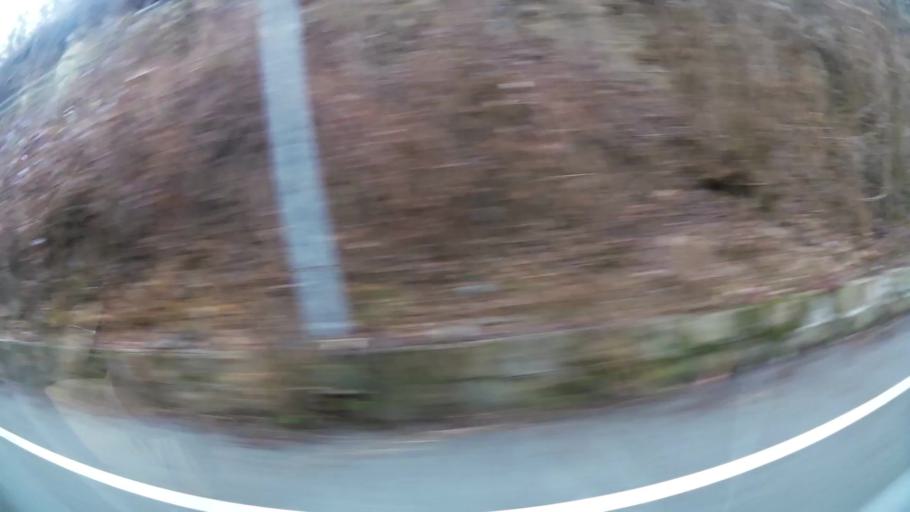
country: BG
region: Sofia-Capital
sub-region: Stolichna Obshtina
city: Sofia
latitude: 42.5873
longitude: 23.4266
